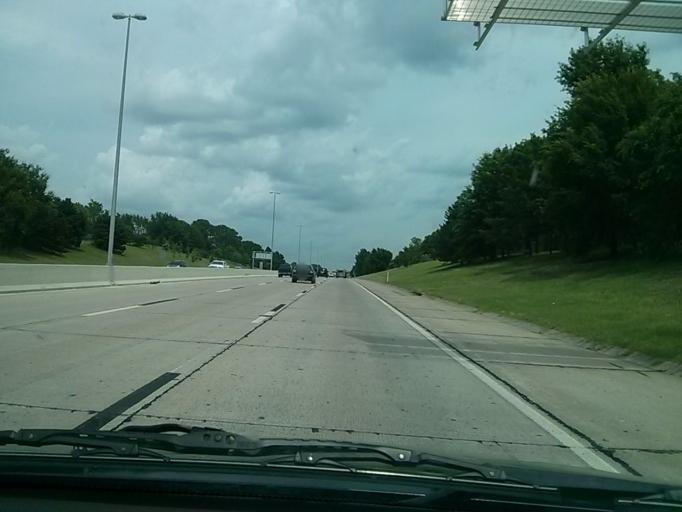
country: US
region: Oklahoma
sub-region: Tulsa County
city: Jenks
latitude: 36.0252
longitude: -95.9362
